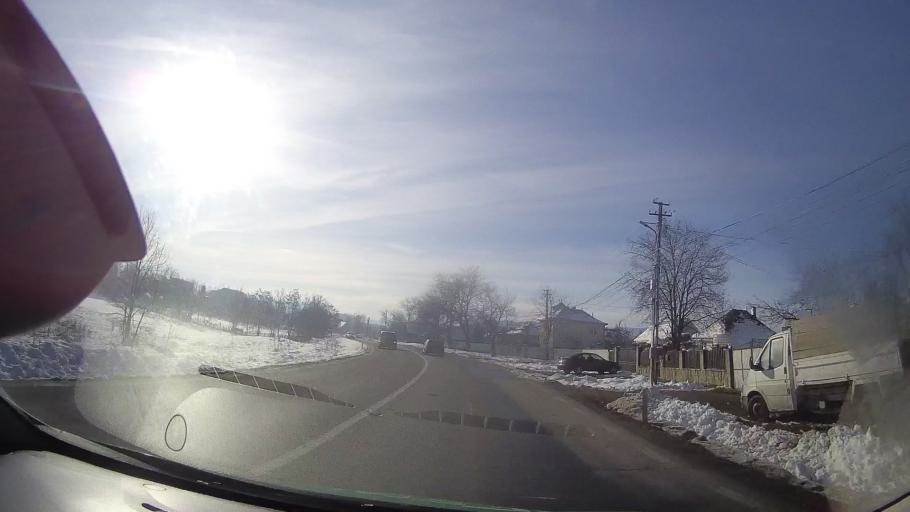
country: RO
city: Vanatori-Neamt
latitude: 47.1836
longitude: 26.3325
